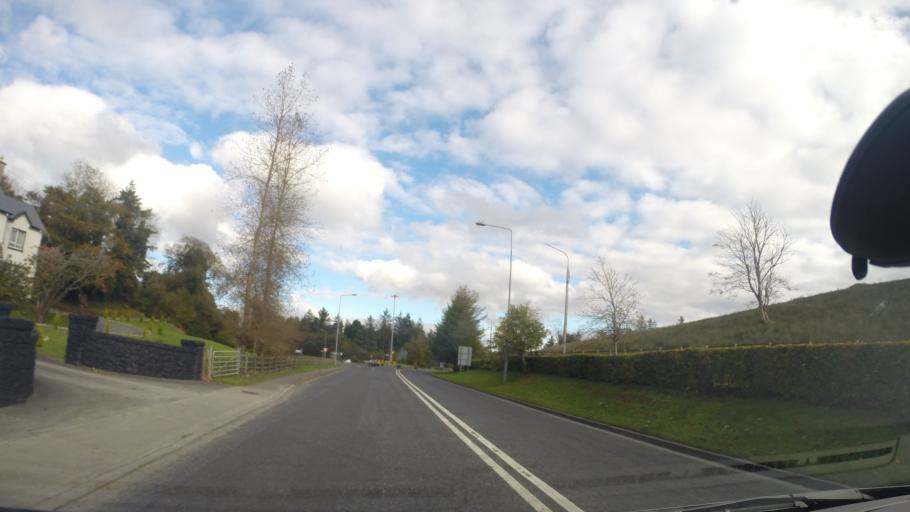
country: IE
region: Ulster
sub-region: County Donegal
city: Donegal
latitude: 54.6563
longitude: -8.1214
